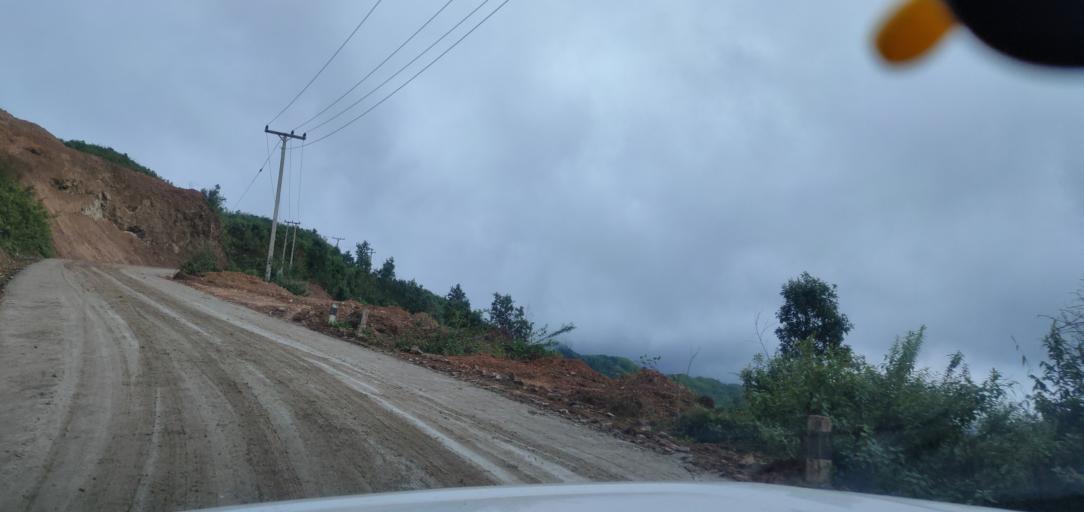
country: LA
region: Phongsali
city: Phongsali
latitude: 21.4228
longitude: 102.1742
